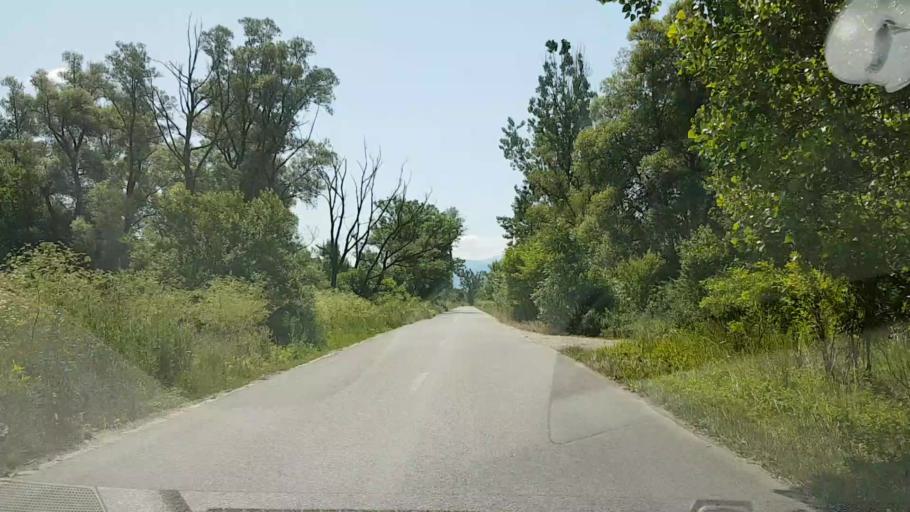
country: RO
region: Brasov
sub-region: Comuna Voila
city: Voila
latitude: 45.8559
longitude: 24.8295
